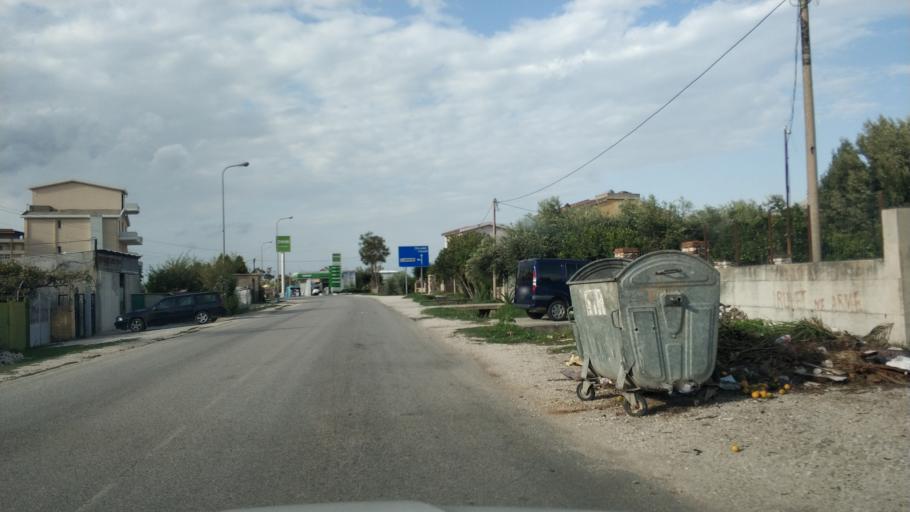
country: AL
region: Vlore
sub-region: Rrethi i Vlores
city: Orikum
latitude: 40.3280
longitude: 19.4784
